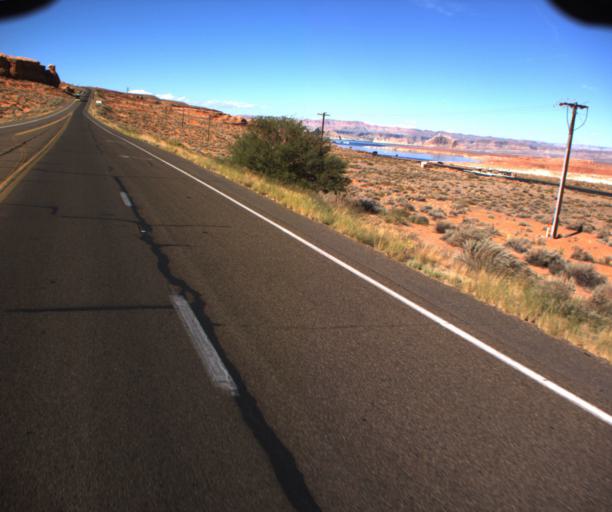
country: US
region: Arizona
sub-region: Coconino County
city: Page
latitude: 36.9405
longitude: -111.4951
